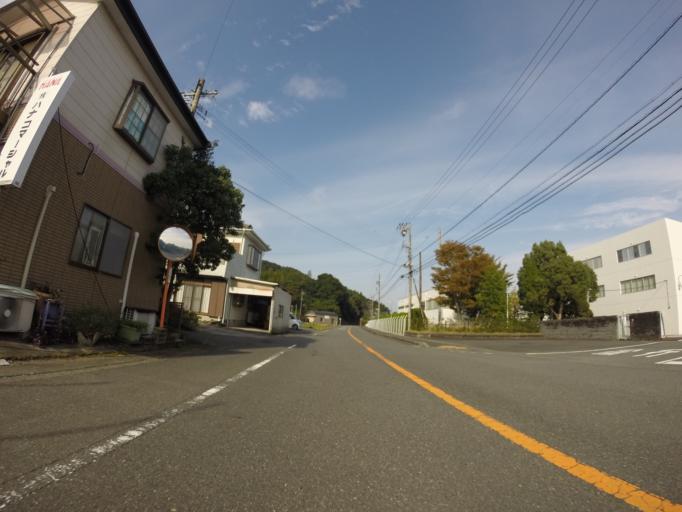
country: JP
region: Shizuoka
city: Shimada
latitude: 34.7591
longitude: 138.1940
